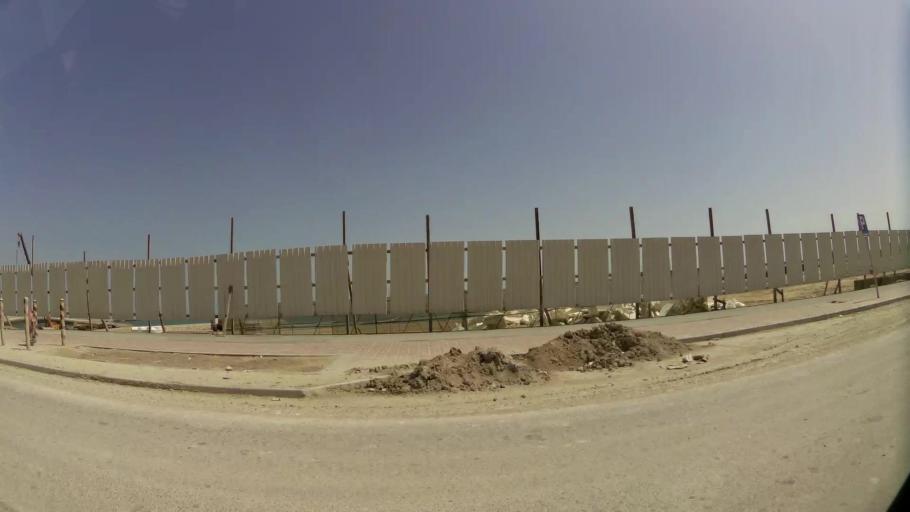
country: QA
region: Baladiyat Umm Salal
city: Umm Salal Muhammad
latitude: 25.4042
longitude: 51.5237
